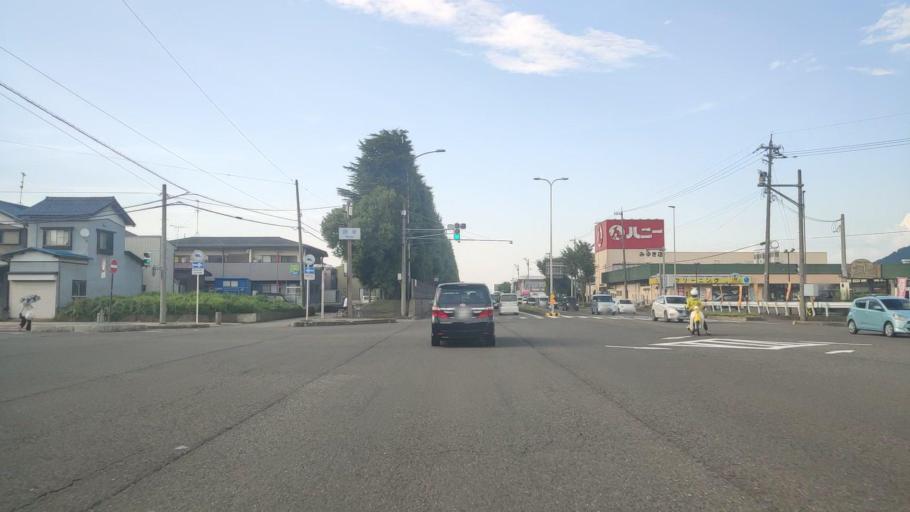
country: JP
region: Fukui
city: Sabae
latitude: 35.9749
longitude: 136.1933
